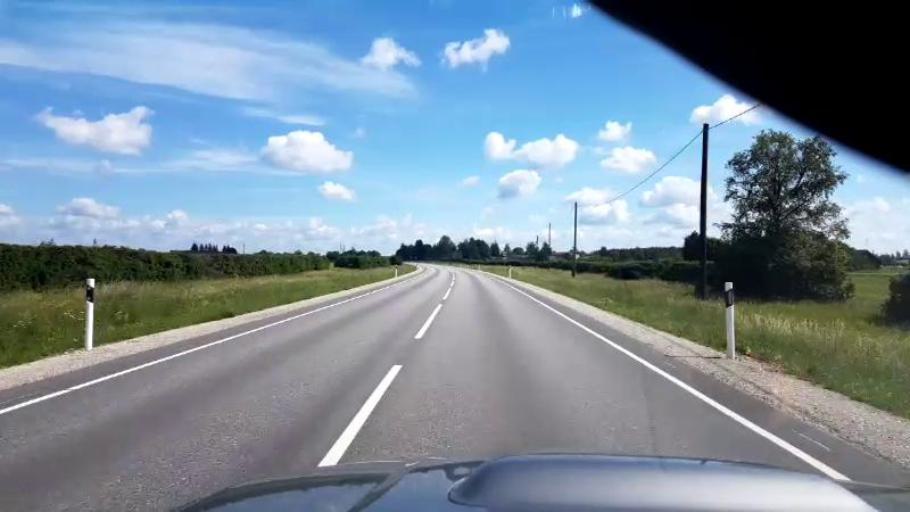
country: EE
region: Jaervamaa
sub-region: Jaerva-Jaani vald
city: Jarva-Jaani
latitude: 59.1063
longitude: 25.7165
